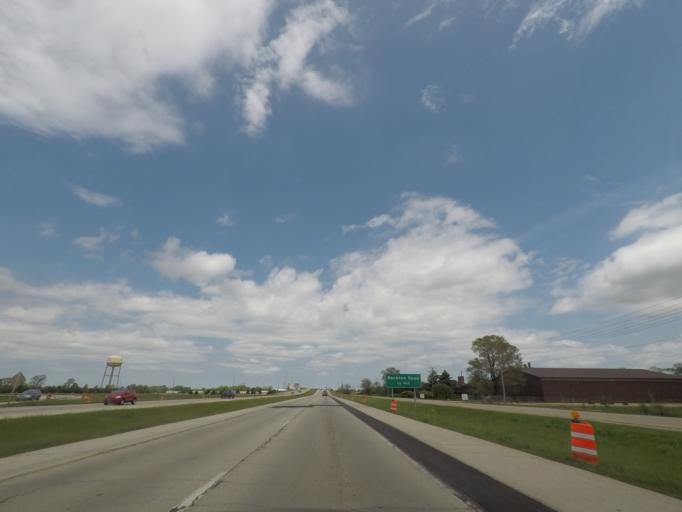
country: US
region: Illinois
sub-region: Winnebago County
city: Roscoe
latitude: 42.4517
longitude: -89.0193
